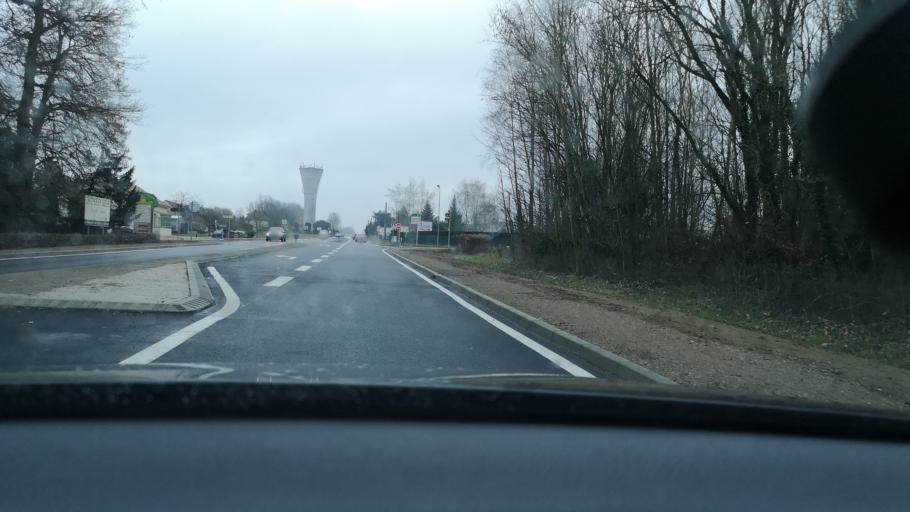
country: FR
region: Bourgogne
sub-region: Departement de Saone-et-Loire
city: Saint-Marcel
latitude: 46.7881
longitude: 4.9152
